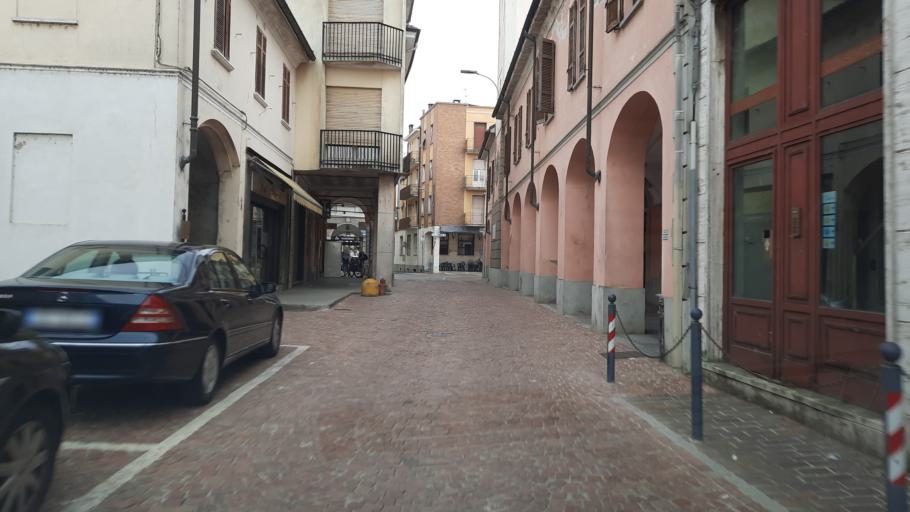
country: IT
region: Lombardy
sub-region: Provincia di Pavia
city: Robbio
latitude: 45.2903
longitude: 8.5934
